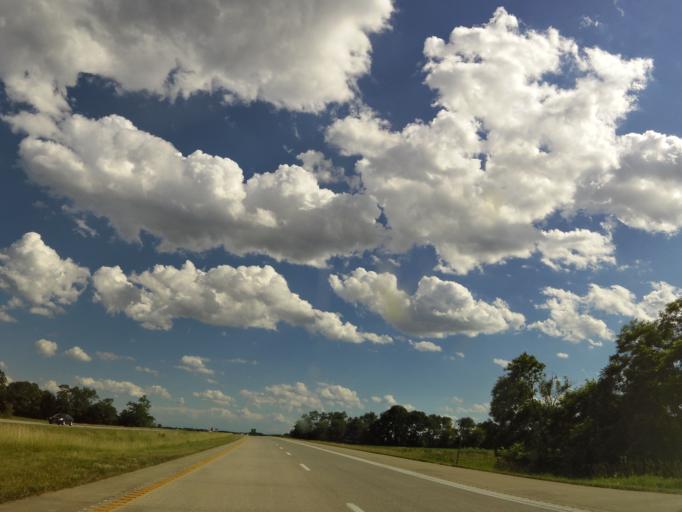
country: US
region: Missouri
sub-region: Clark County
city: Kahoka
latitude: 40.4190
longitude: -91.5728
